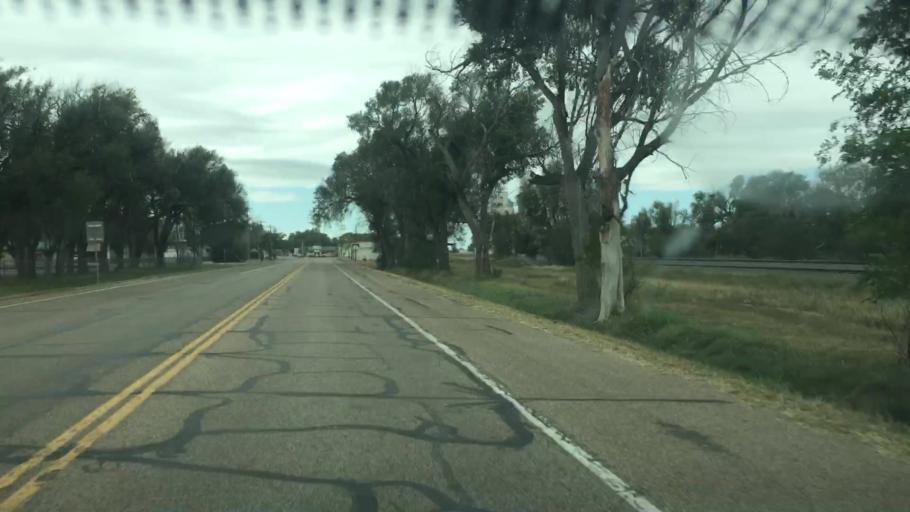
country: US
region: Colorado
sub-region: Prowers County
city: Lamar
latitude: 38.0620
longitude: -102.3045
